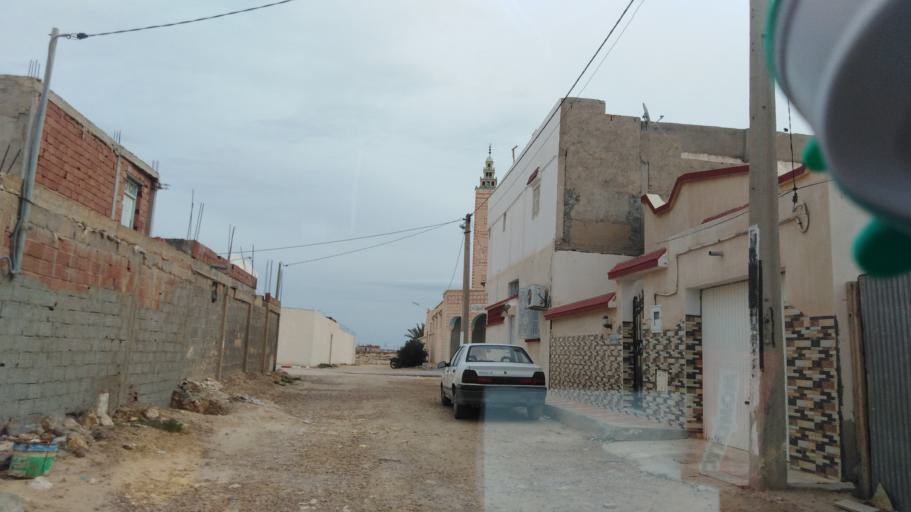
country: TN
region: Qabis
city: Gabes
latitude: 33.9509
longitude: 10.0045
